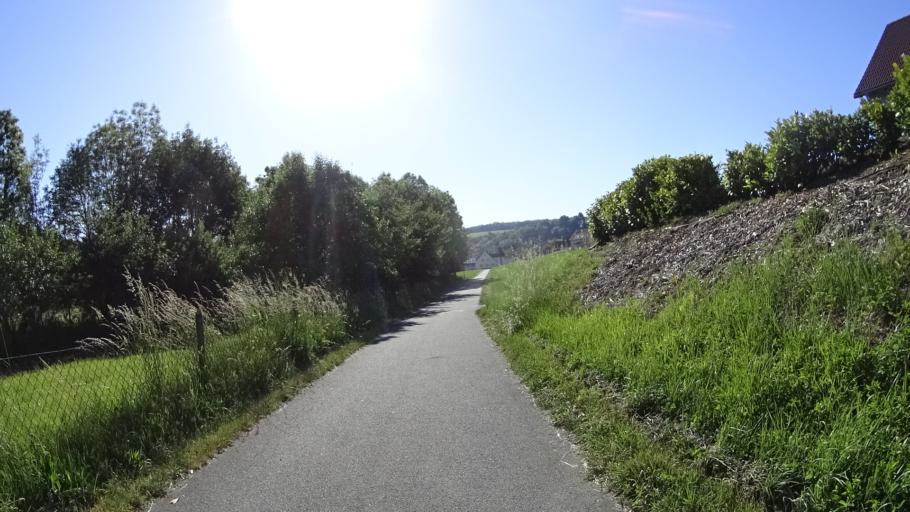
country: DE
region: Baden-Wuerttemberg
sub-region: Regierungsbezirk Stuttgart
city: Boxberg
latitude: 49.4837
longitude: 9.6287
